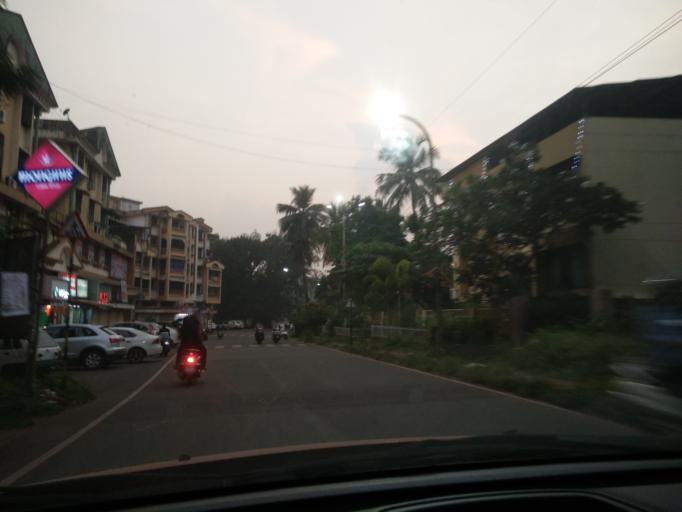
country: IN
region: Goa
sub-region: South Goa
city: Madgaon
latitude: 15.2733
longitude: 73.9725
